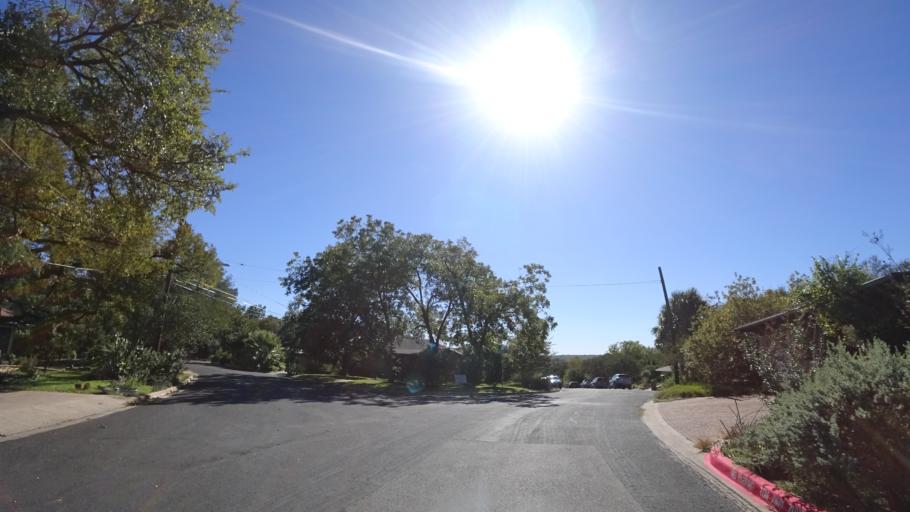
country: US
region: Texas
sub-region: Travis County
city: Austin
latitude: 30.2752
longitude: -97.7583
